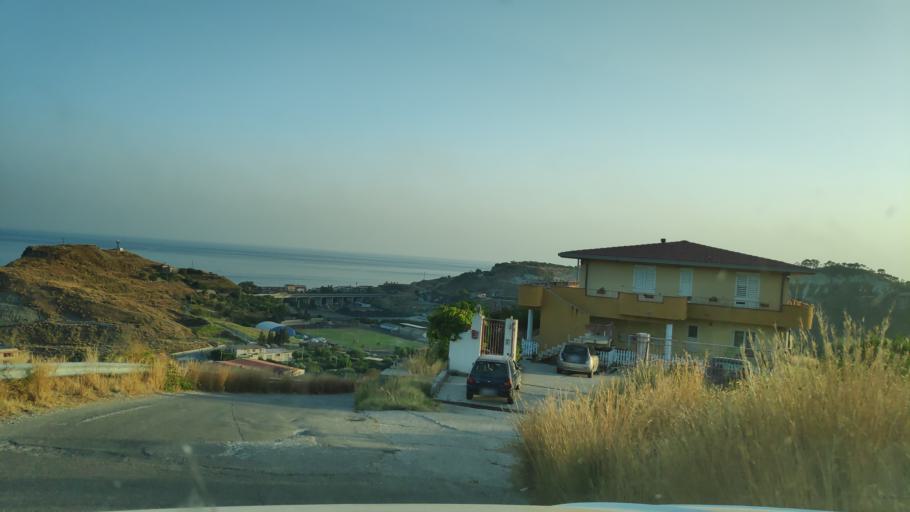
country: IT
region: Calabria
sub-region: Provincia di Reggio Calabria
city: Bova Marina
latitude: 37.9405
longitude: 15.9143
